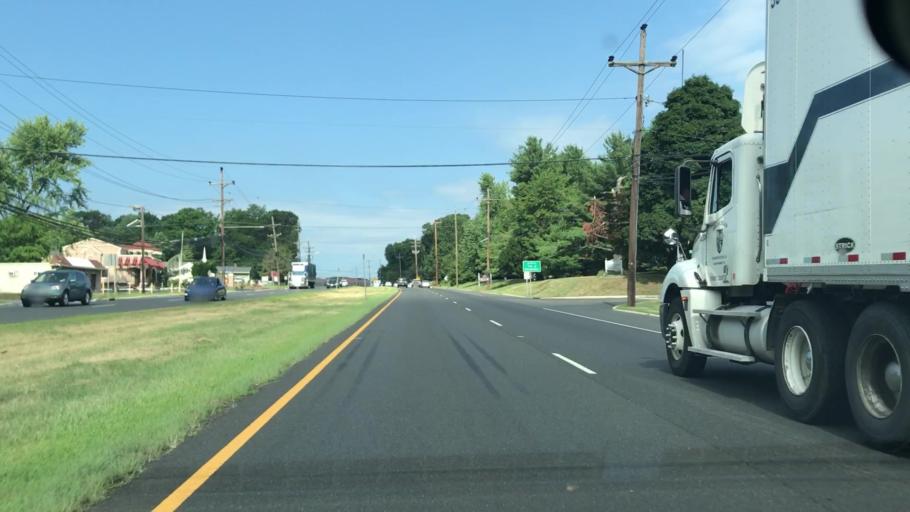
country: US
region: New Jersey
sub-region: Somerset County
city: Bradley Gardens
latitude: 40.5746
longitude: -74.6578
